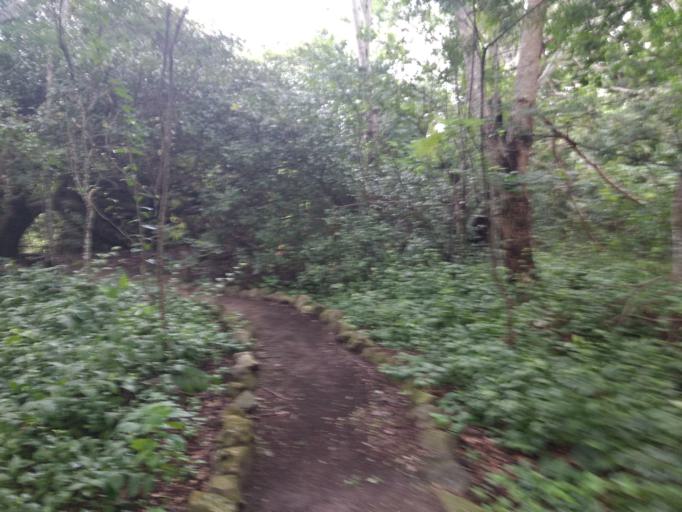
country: BR
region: Ceara
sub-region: Crateus
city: Crateus
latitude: -5.1418
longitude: -40.9171
